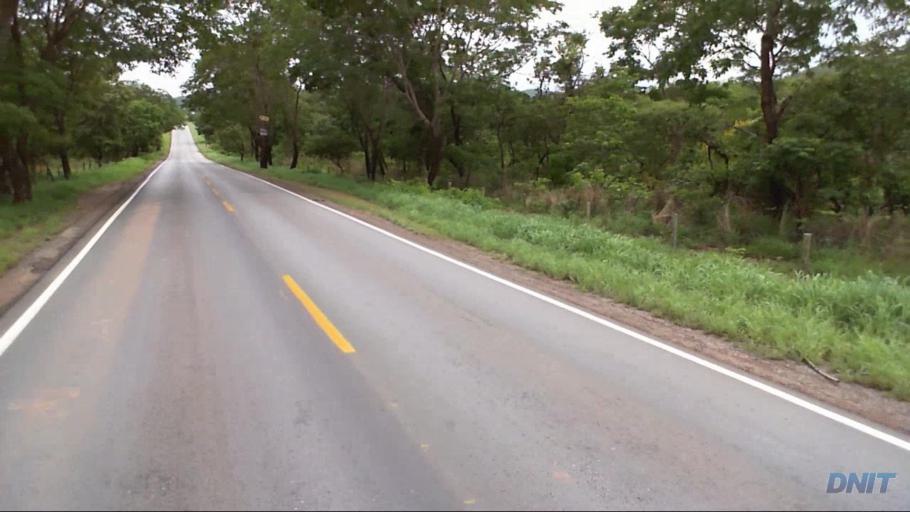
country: BR
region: Goias
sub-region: Padre Bernardo
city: Padre Bernardo
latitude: -15.4490
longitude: -48.2061
